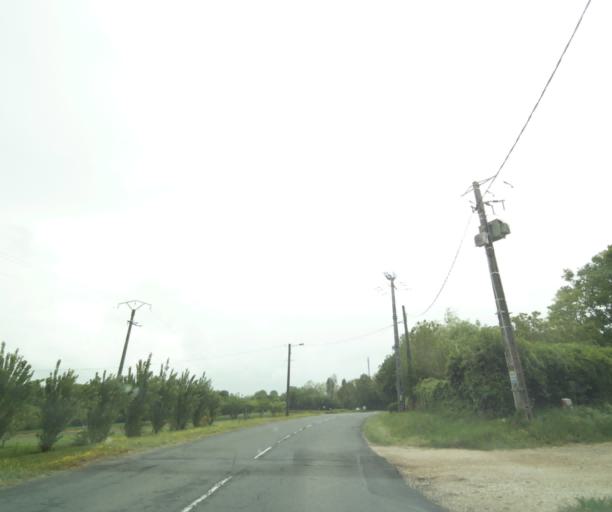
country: FR
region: Poitou-Charentes
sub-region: Departement de la Charente-Maritime
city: Chaniers
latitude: 45.7624
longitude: -0.5340
